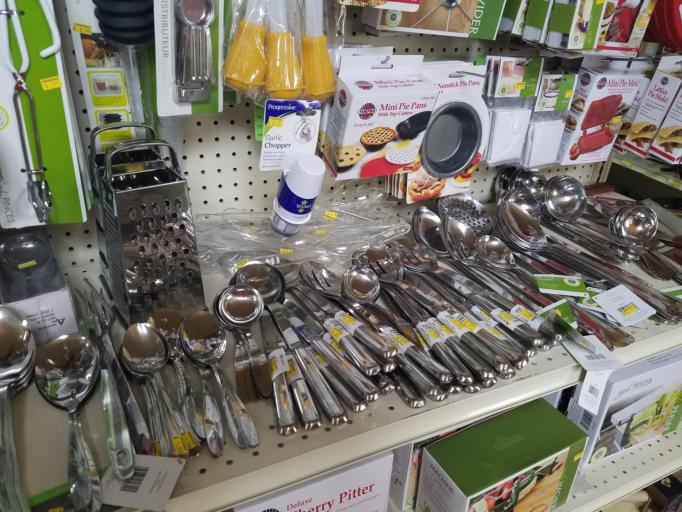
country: US
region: Michigan
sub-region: Osceola County
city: Evart
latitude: 44.1041
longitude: -85.1480
